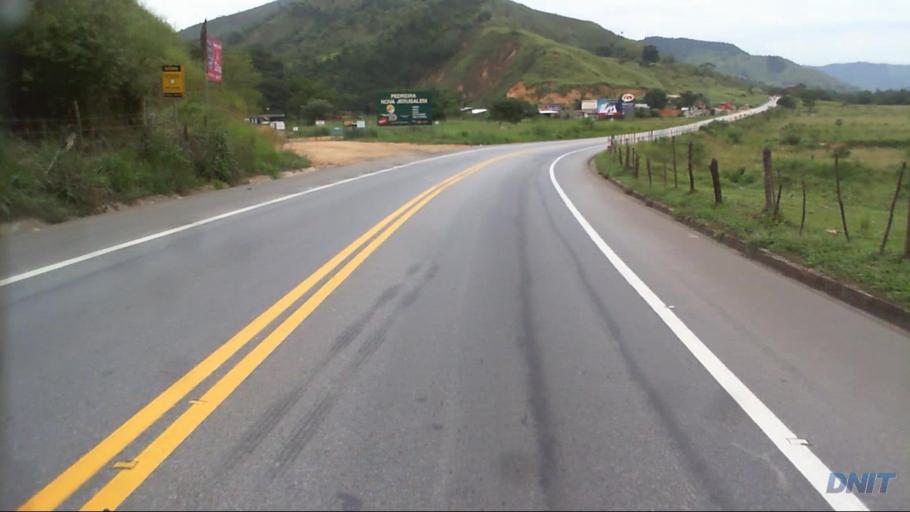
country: BR
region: Minas Gerais
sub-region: Timoteo
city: Timoteo
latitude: -19.5837
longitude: -42.7287
